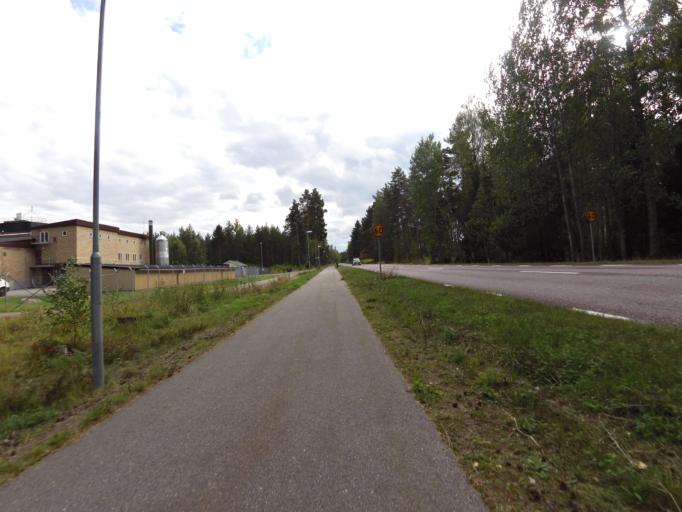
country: SE
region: Gaevleborg
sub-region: Sandvikens Kommun
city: Sandviken
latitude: 60.6883
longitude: 16.8145
